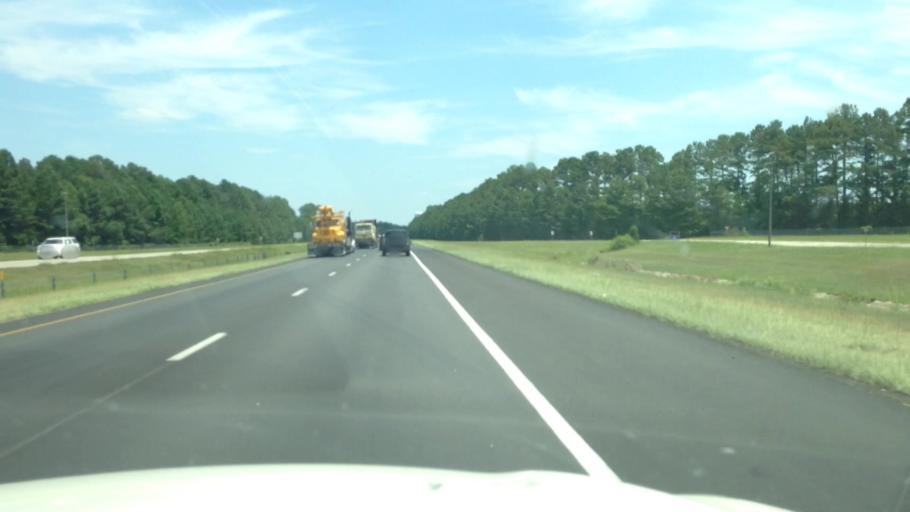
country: US
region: South Carolina
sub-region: Florence County
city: Timmonsville
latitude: 34.2045
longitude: -80.0545
